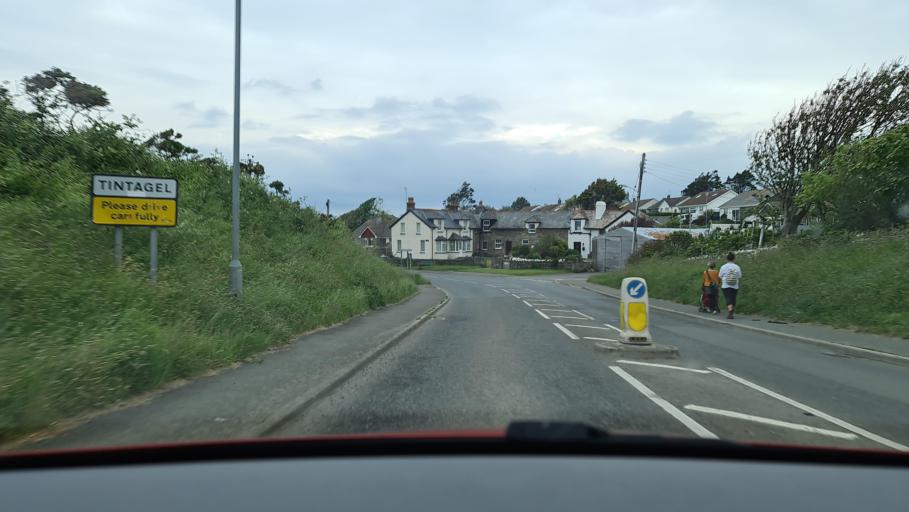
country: GB
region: England
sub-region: Cornwall
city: Tintagel
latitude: 50.6597
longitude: -4.7493
